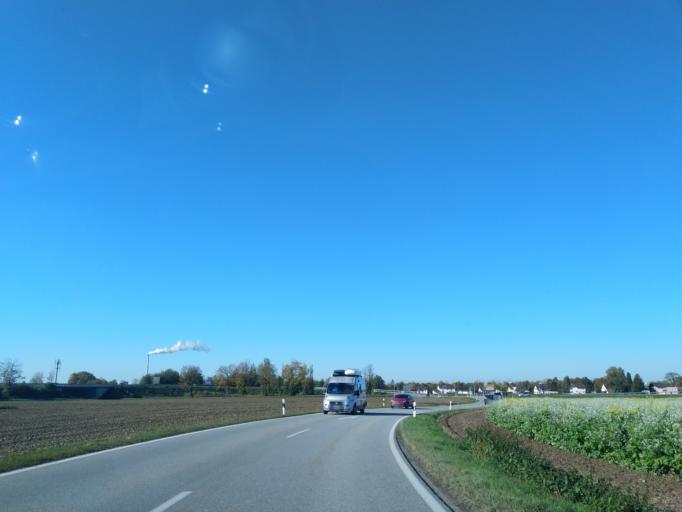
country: DE
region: Bavaria
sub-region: Lower Bavaria
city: Plattling
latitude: 48.7986
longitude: 12.9070
